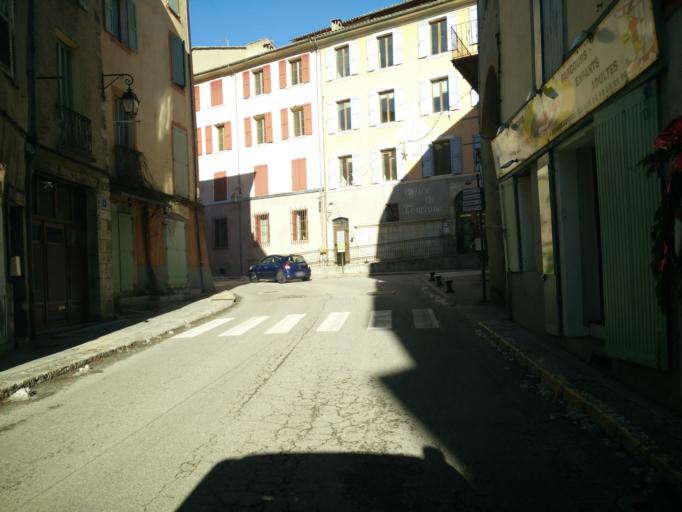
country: FR
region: Provence-Alpes-Cote d'Azur
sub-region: Departement des Alpes-de-Haute-Provence
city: Castellane
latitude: 43.8474
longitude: 6.5121
